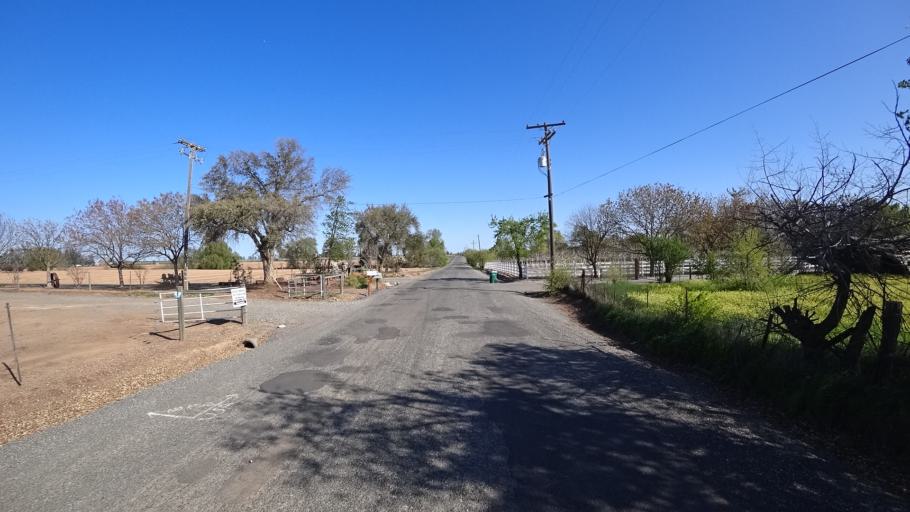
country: US
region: California
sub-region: Glenn County
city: Hamilton City
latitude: 39.7858
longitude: -122.0665
